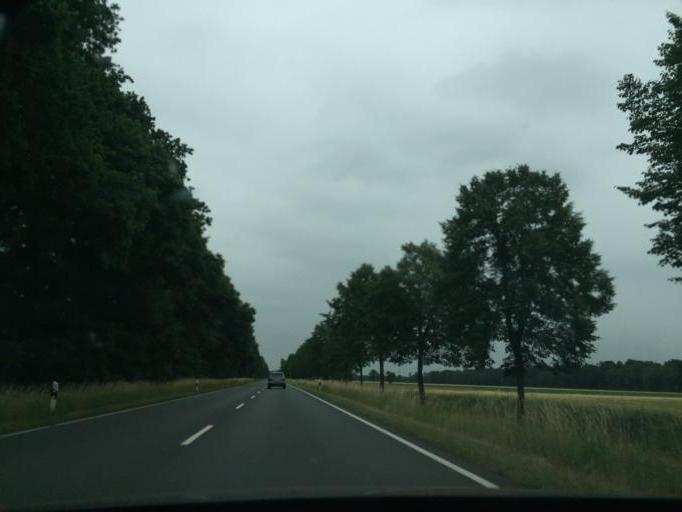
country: DE
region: North Rhine-Westphalia
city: Lengerich
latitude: 52.1206
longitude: 7.8276
